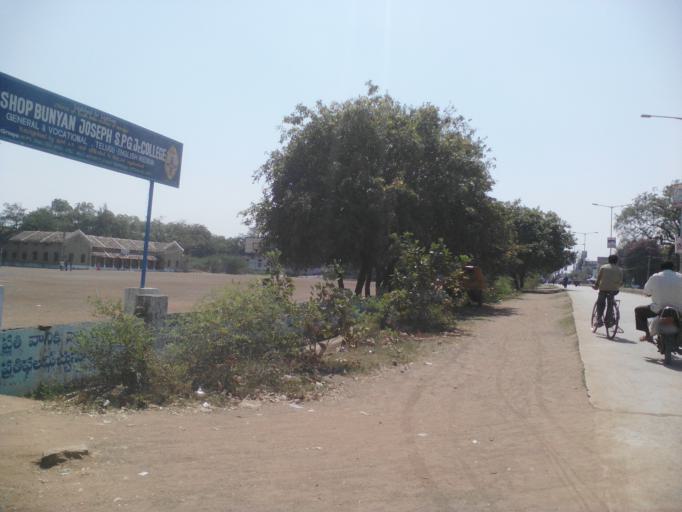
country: IN
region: Andhra Pradesh
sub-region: Kurnool
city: Nandyal
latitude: 15.4805
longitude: 78.4711
